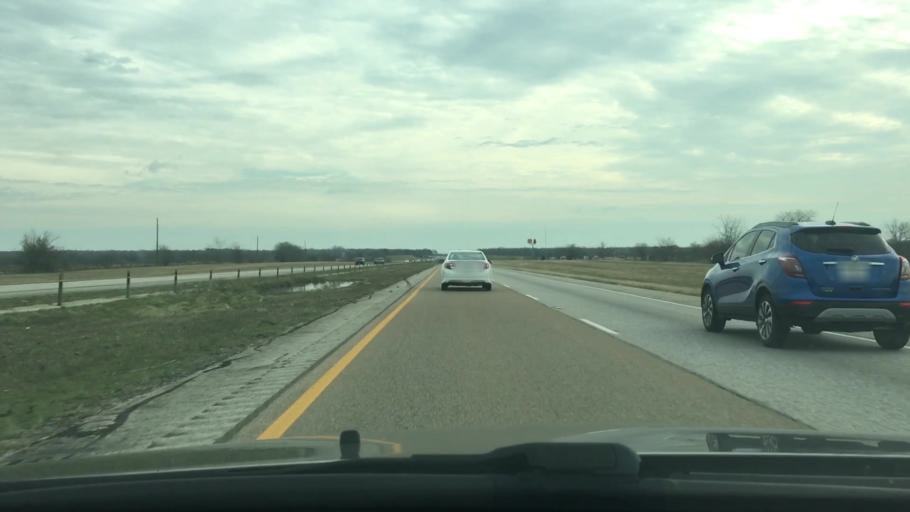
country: US
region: Texas
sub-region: Leon County
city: Centerville
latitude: 31.1021
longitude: -95.9644
